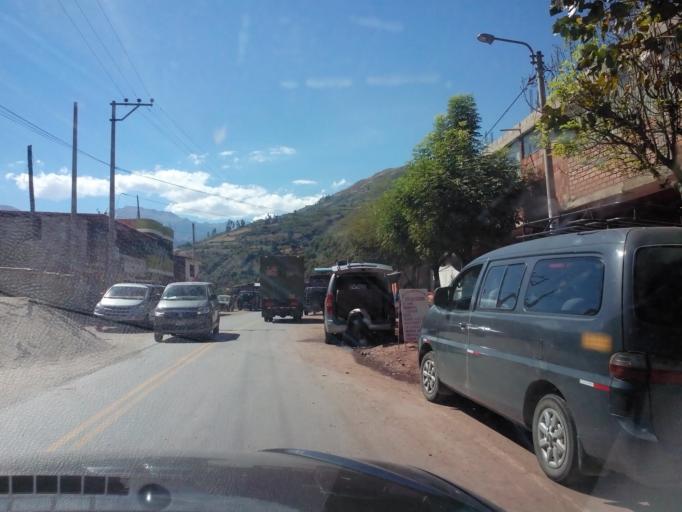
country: PE
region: Cusco
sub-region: Provincia de Anta
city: Limatambo
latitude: -13.4794
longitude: -72.4452
